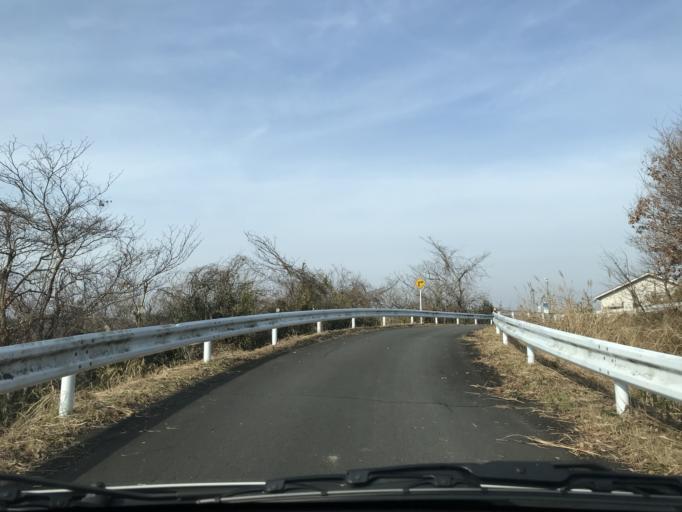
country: JP
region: Miyagi
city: Wakuya
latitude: 38.7043
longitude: 141.1538
